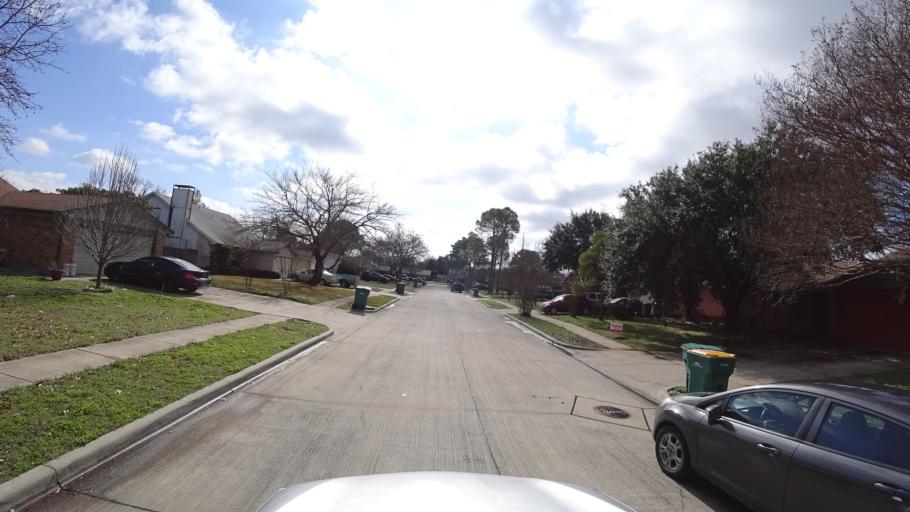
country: US
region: Texas
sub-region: Denton County
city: Lewisville
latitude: 33.0293
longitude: -97.0062
